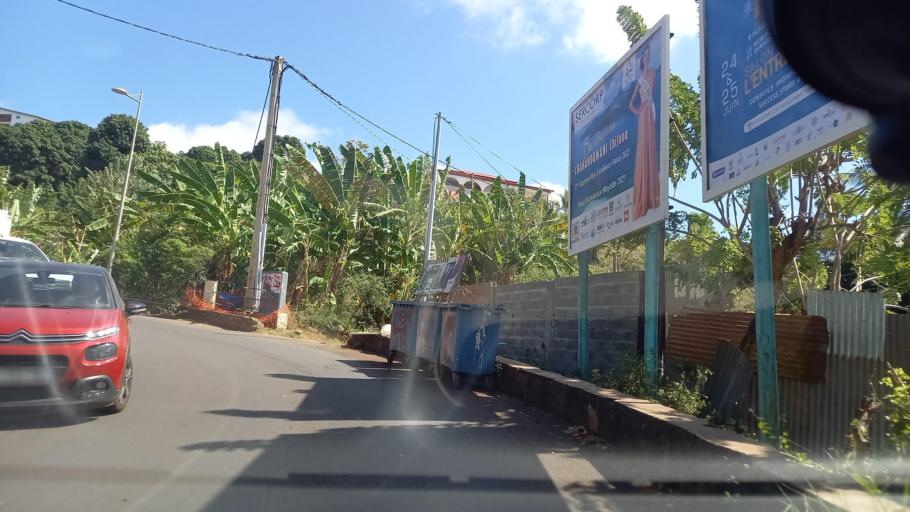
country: YT
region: Mamoudzou
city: Mamoudzou
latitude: -12.7772
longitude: 45.2241
